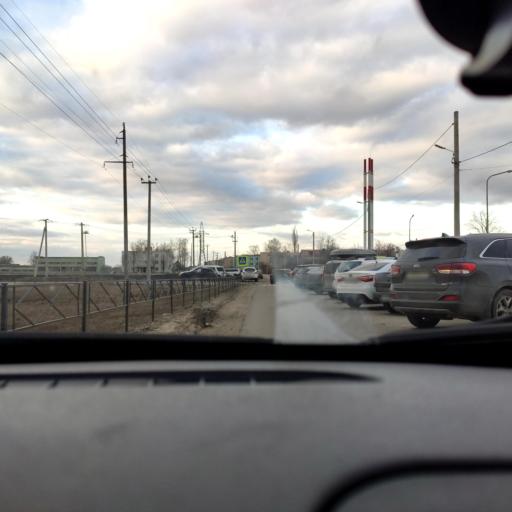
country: RU
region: Voronezj
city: Ramon'
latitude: 51.9132
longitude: 39.3294
